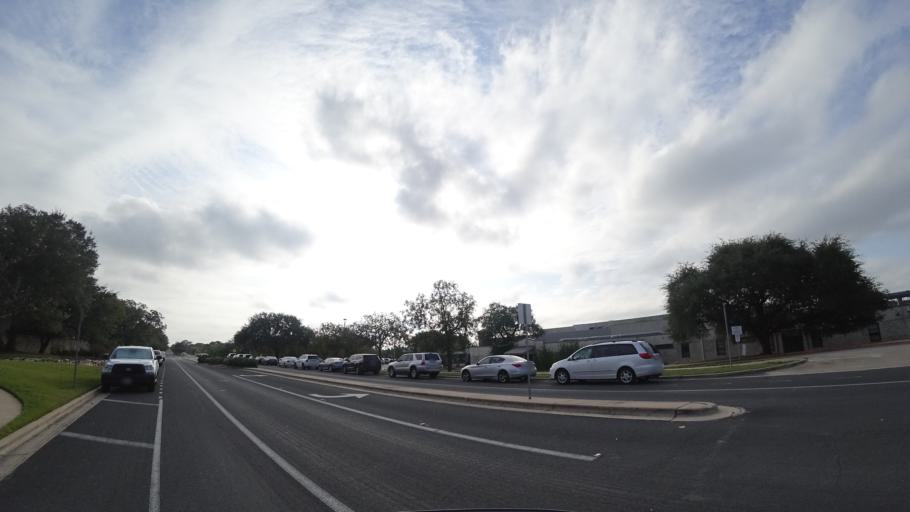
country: US
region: Texas
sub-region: Travis County
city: Shady Hollow
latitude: 30.1923
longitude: -97.8816
